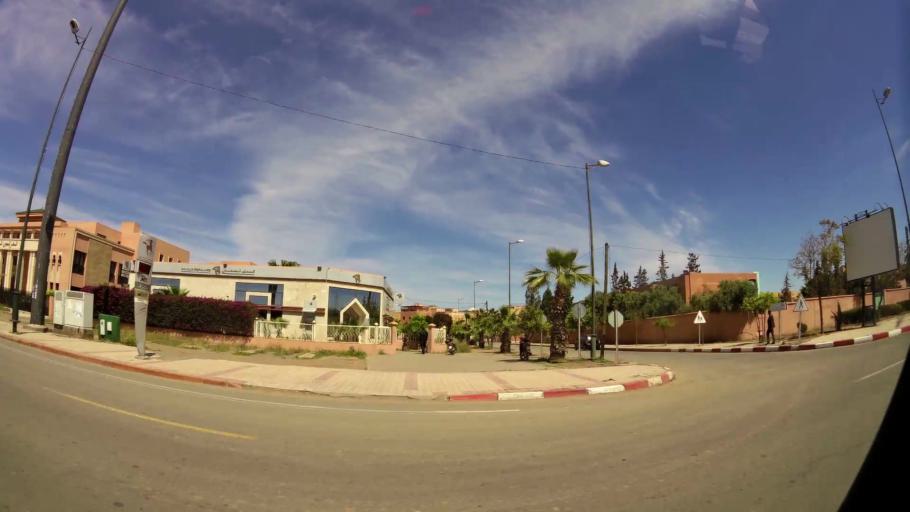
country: MA
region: Marrakech-Tensift-Al Haouz
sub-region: Marrakech
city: Marrakesh
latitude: 31.6099
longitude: -7.9738
